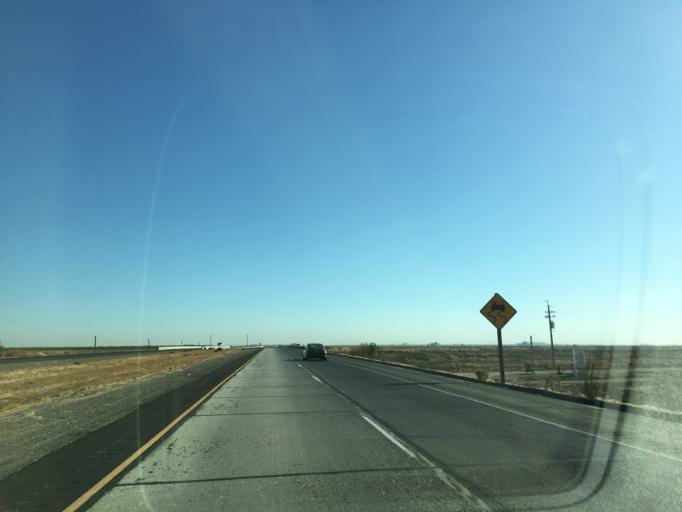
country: US
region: California
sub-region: Merced County
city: Dos Palos
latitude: 37.0717
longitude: -120.5219
